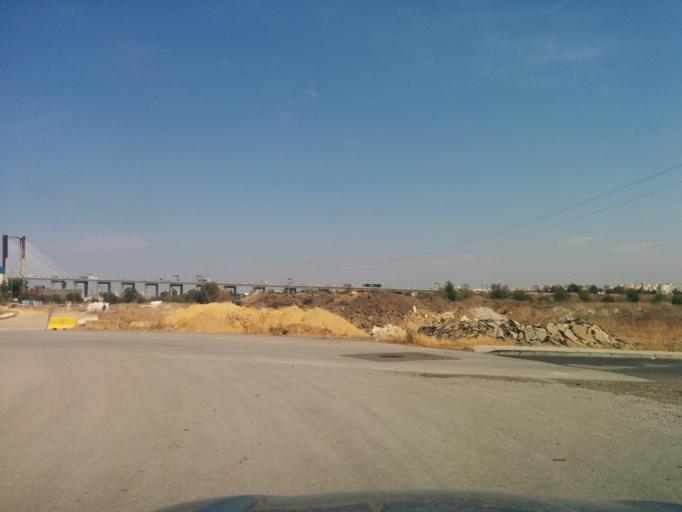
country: ES
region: Andalusia
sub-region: Provincia de Sevilla
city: Gelves
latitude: 37.3393
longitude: -5.9898
